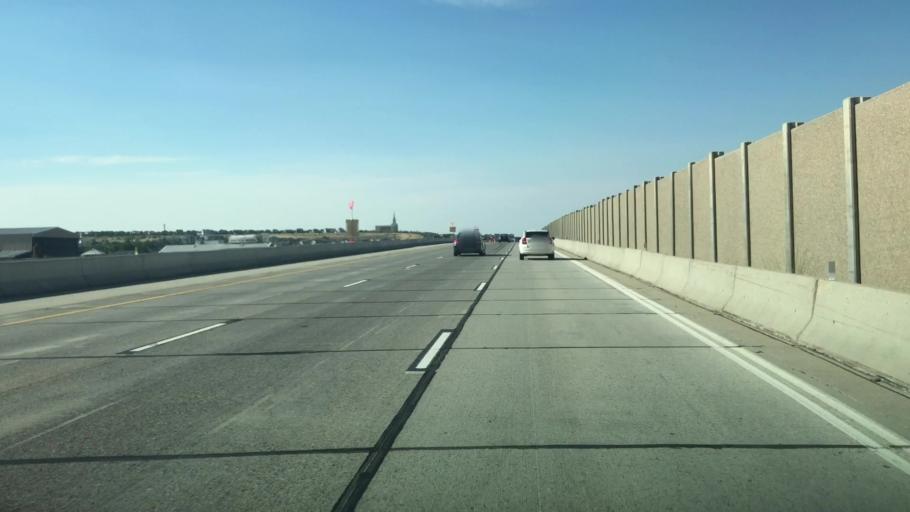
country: US
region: Utah
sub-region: Salt Lake County
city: South Jordan Heights
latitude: 40.5343
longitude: -111.9839
